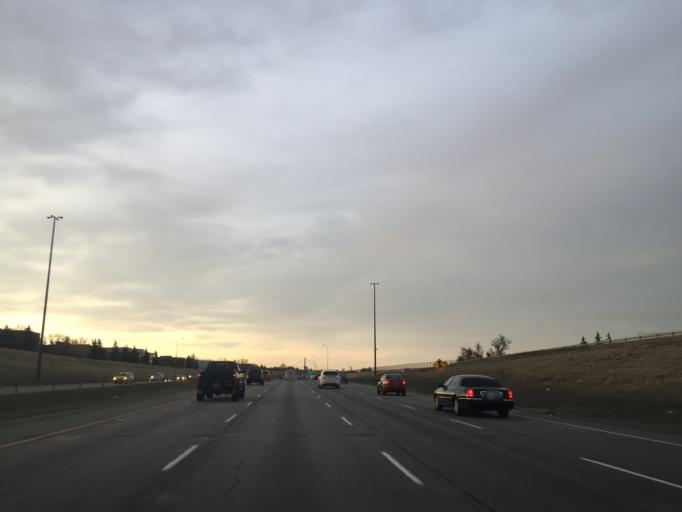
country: CA
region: Alberta
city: Calgary
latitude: 51.0808
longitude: -114.0335
